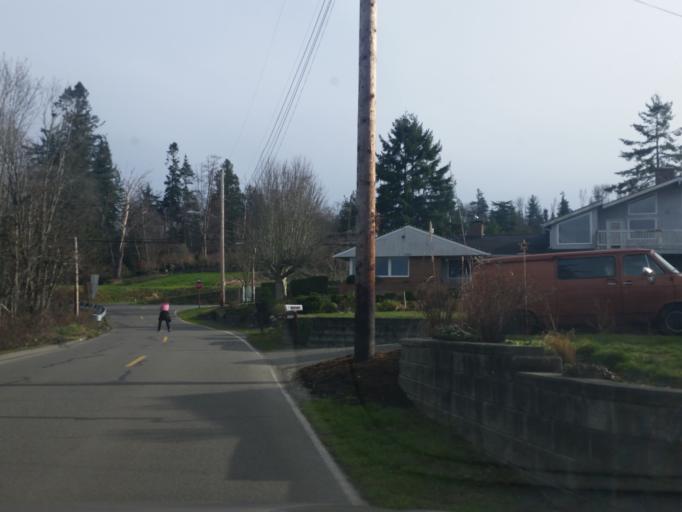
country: US
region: Washington
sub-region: Snohomish County
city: Mukilteo
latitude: 47.9512
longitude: -122.2877
